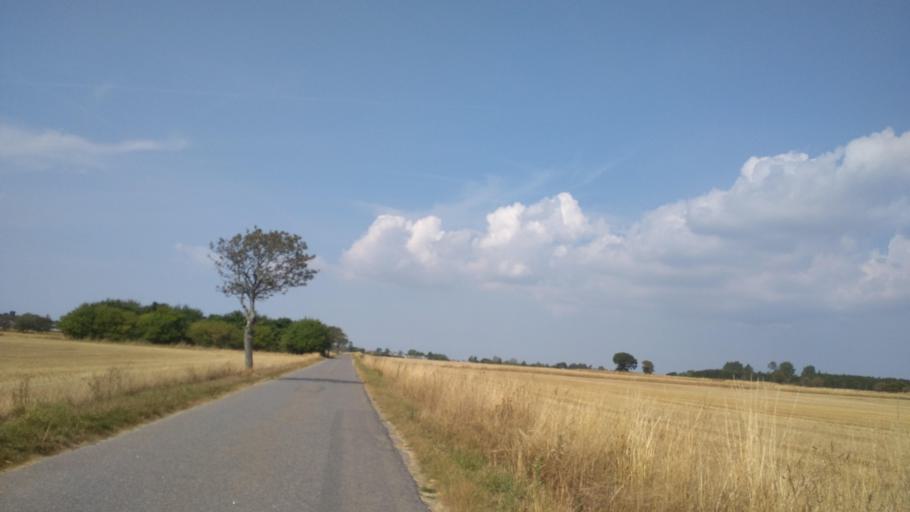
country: DK
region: Capital Region
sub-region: Bornholm Kommune
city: Akirkeby
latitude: 55.0640
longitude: 14.9369
